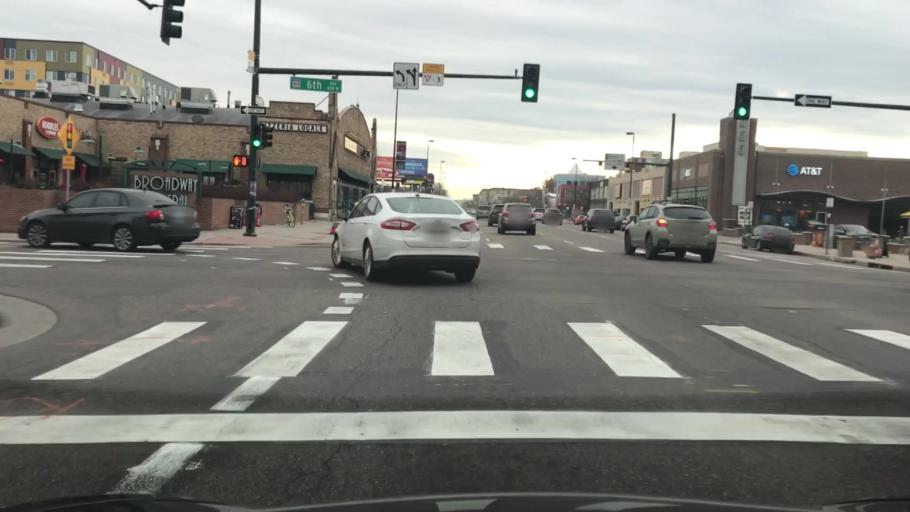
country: US
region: Colorado
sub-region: Denver County
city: Denver
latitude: 39.7258
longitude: -104.9874
